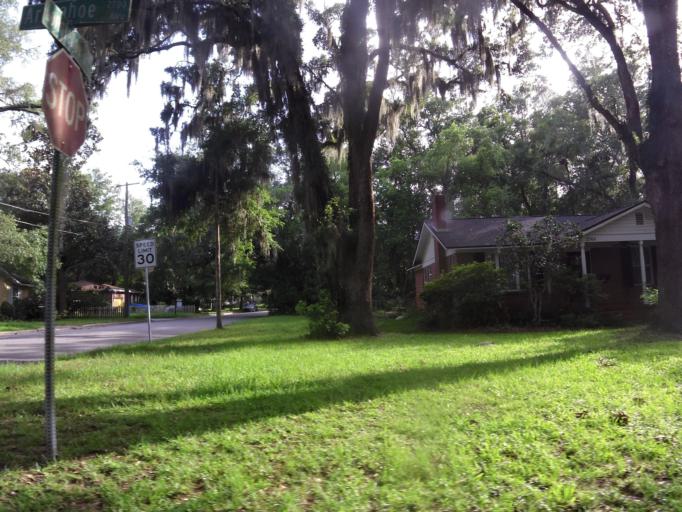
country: US
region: Florida
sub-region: Duval County
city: Jacksonville
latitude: 30.2714
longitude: -81.7078
